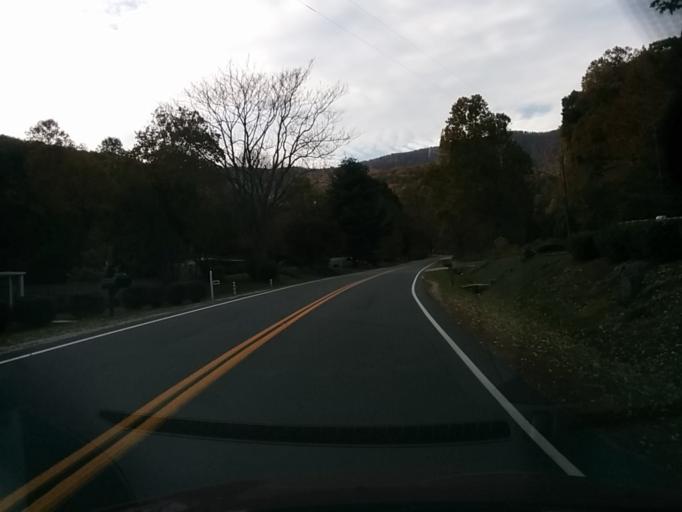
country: US
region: Virginia
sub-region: Nelson County
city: Nellysford
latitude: 37.8819
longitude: -78.9662
